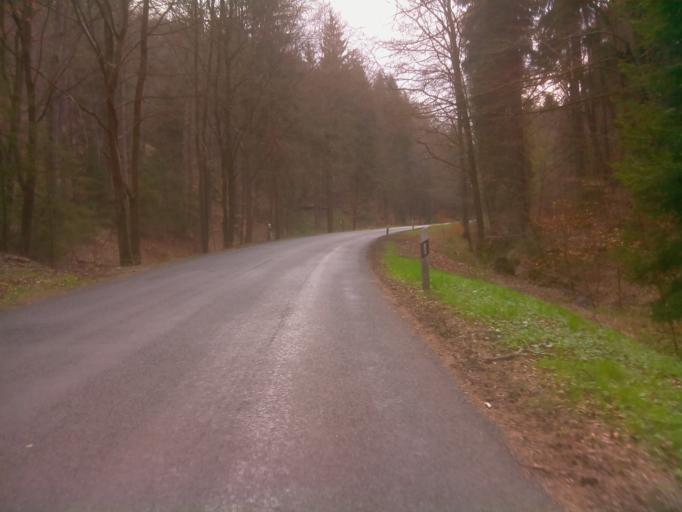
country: DE
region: Thuringia
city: Grosseutersdorf
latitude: 50.7679
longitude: 11.5710
